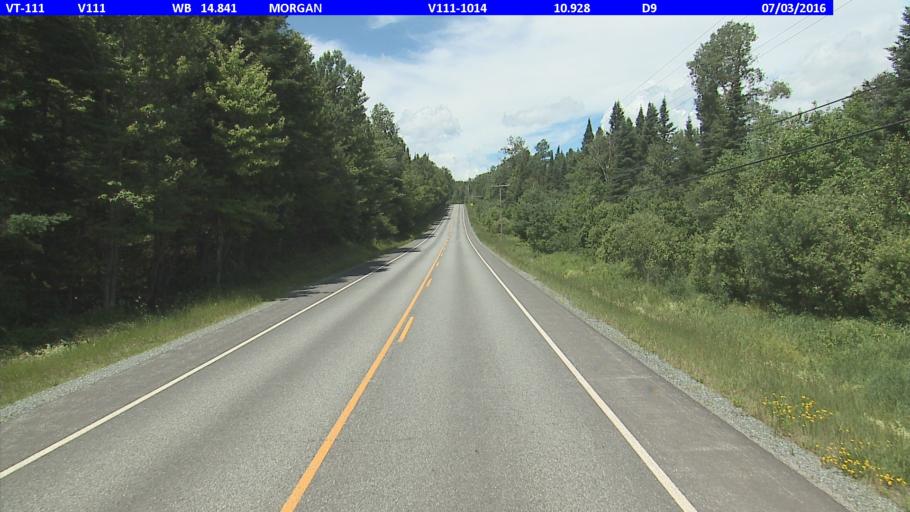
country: US
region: Vermont
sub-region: Orleans County
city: Newport
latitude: 44.8479
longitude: -71.9120
